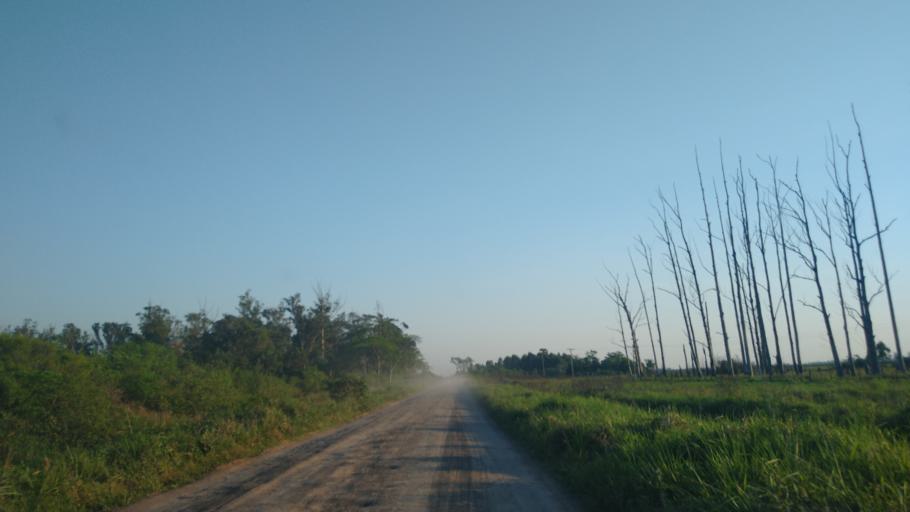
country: PY
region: Neembucu
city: Cerrito
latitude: -27.3994
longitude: -57.6588
